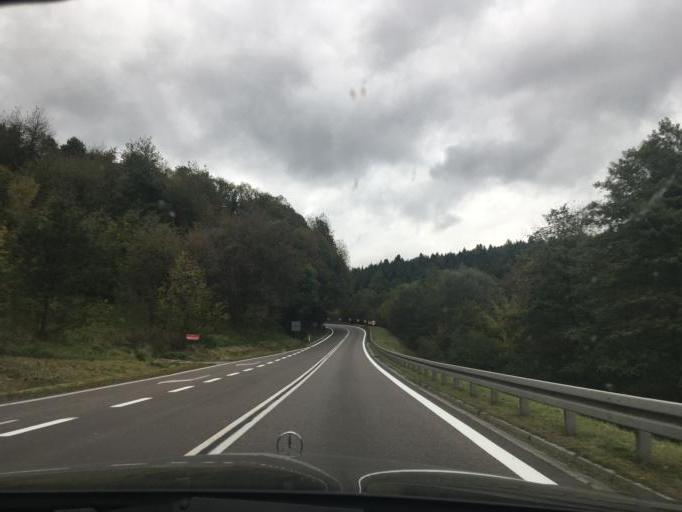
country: PL
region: Subcarpathian Voivodeship
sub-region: Powiat brzozowski
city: Jablonica Polska
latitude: 49.7131
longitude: 21.8970
